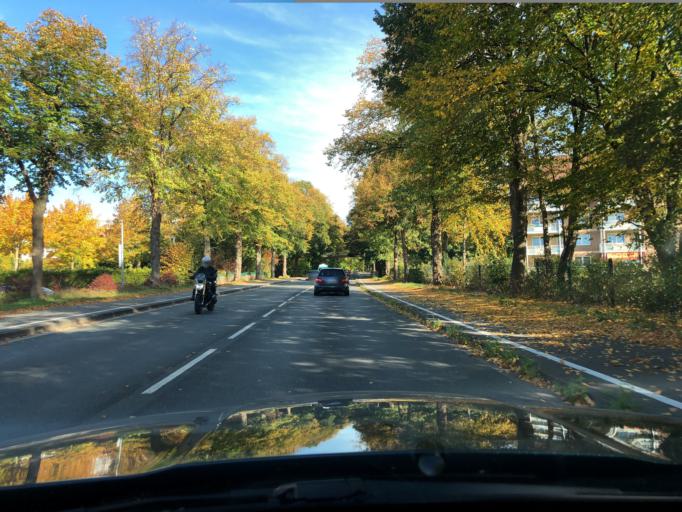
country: DE
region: North Rhine-Westphalia
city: Lengerich
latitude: 52.1828
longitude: 7.8547
